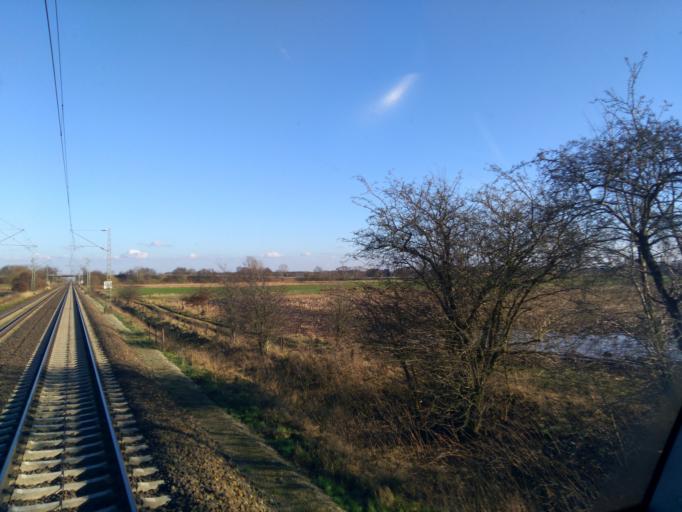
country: DE
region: Lower Saxony
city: Oyten
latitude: 53.0887
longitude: 9.0546
